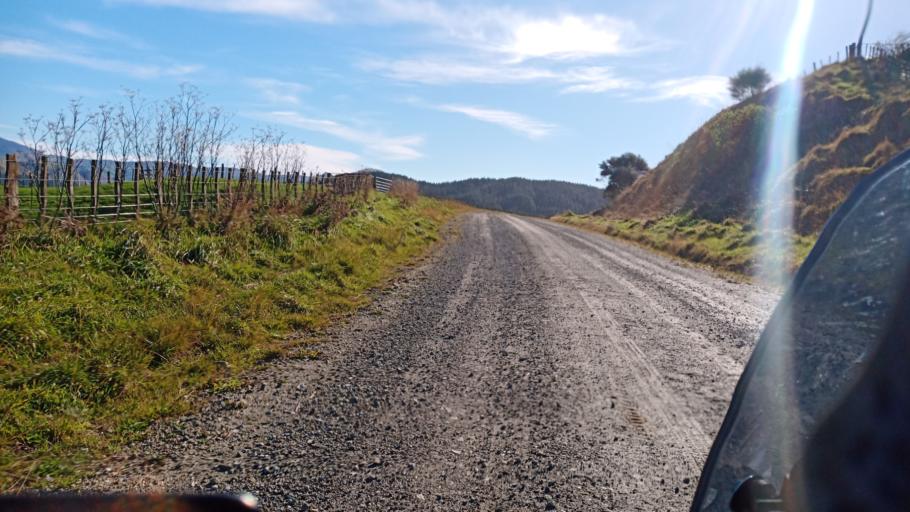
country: NZ
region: Gisborne
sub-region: Gisborne District
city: Gisborne
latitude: -38.3011
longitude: 177.8116
